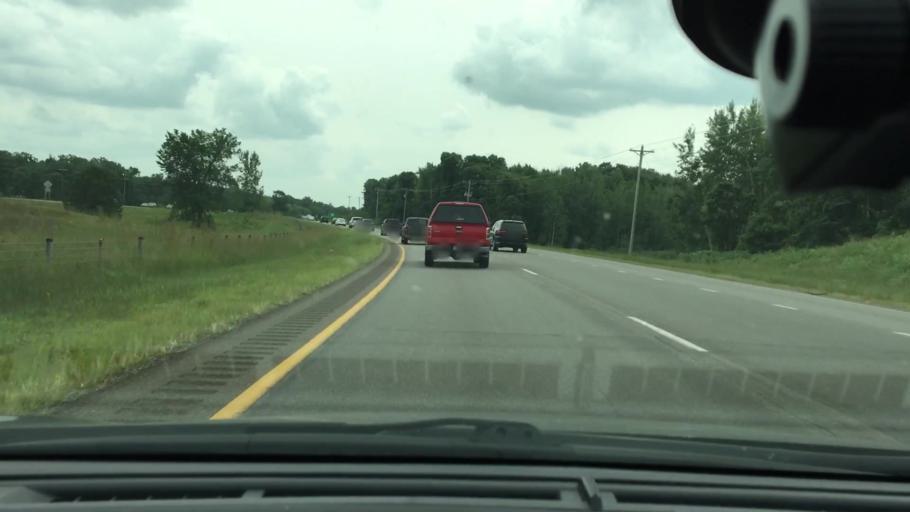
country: US
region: Minnesota
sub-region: Sherburne County
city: Elk River
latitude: 45.3564
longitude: -93.5622
